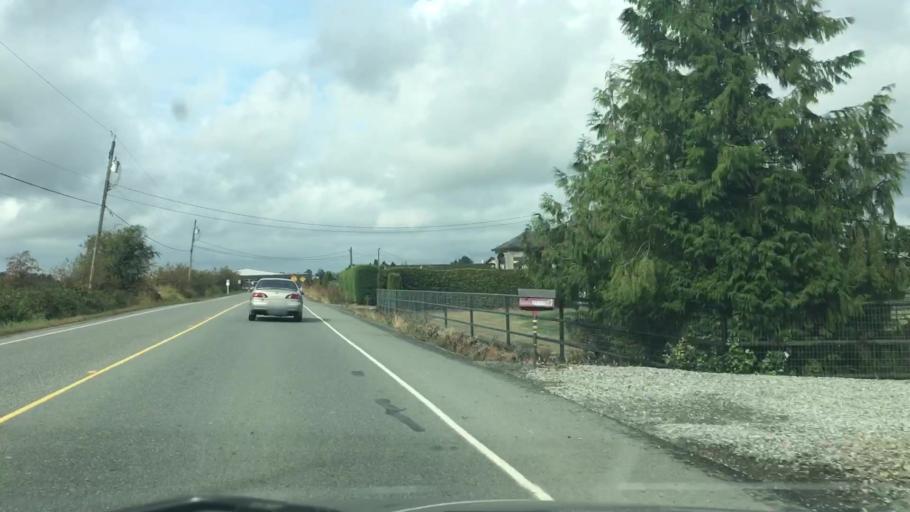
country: CA
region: British Columbia
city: Langley
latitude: 49.1040
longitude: -122.6200
